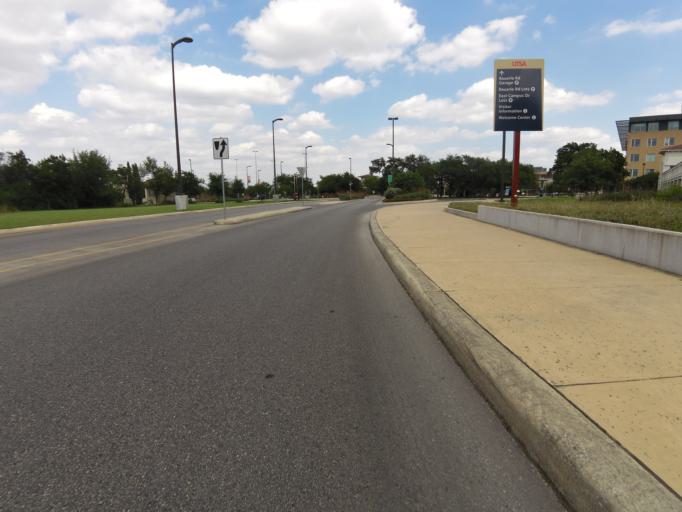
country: US
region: Texas
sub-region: Bexar County
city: Shavano Park
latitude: 29.5874
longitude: -98.6206
